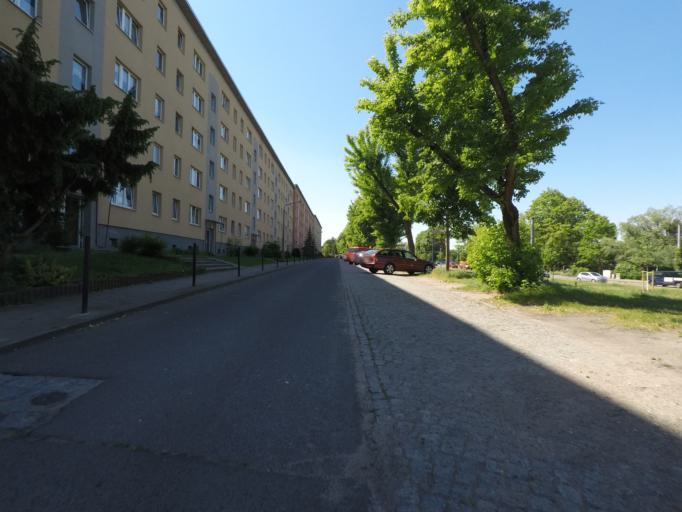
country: DE
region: Brandenburg
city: Eberswalde
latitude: 52.8376
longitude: 13.7507
